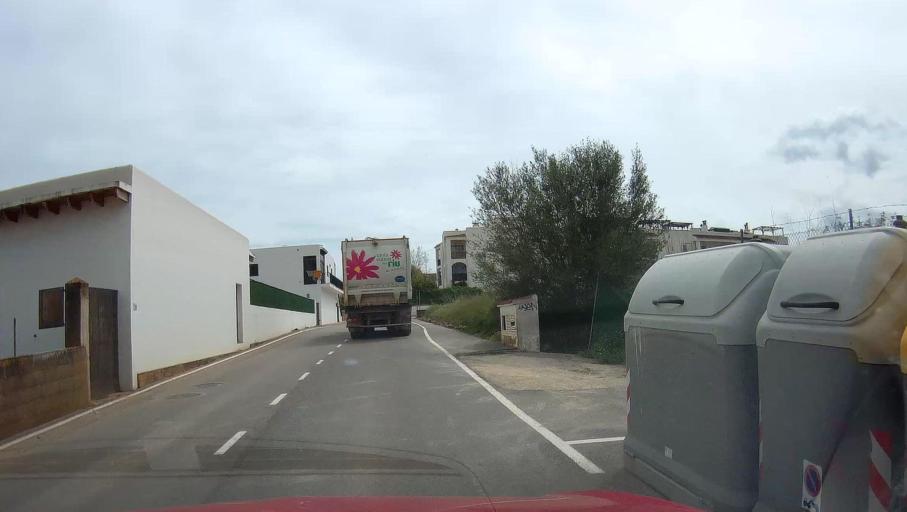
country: ES
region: Balearic Islands
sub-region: Illes Balears
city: Ibiza
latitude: 39.0010
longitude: 1.4292
